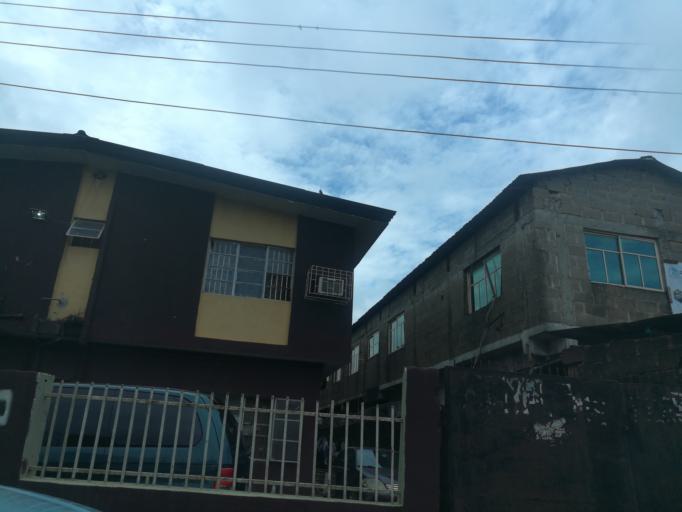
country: NG
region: Lagos
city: Agege
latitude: 6.6218
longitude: 3.3349
